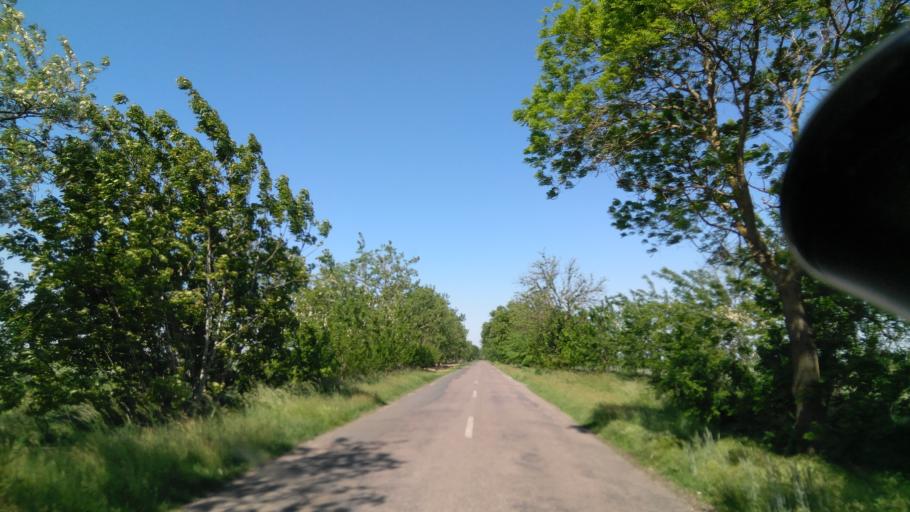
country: HU
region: Bekes
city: Kunagota
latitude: 46.4244
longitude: 21.1024
